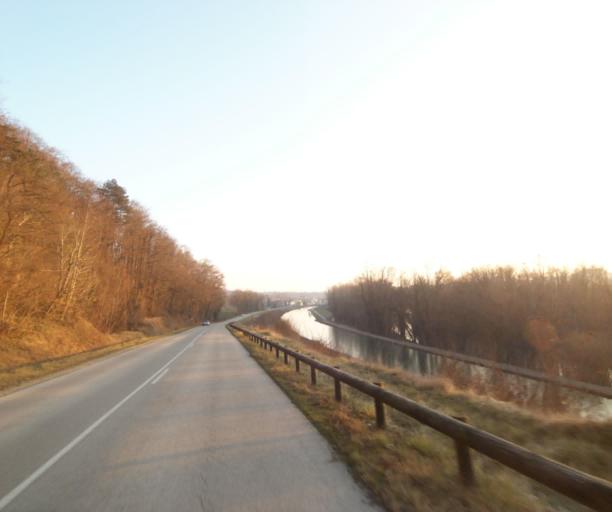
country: FR
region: Champagne-Ardenne
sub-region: Departement de la Haute-Marne
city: Bienville
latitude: 48.5887
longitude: 5.0433
